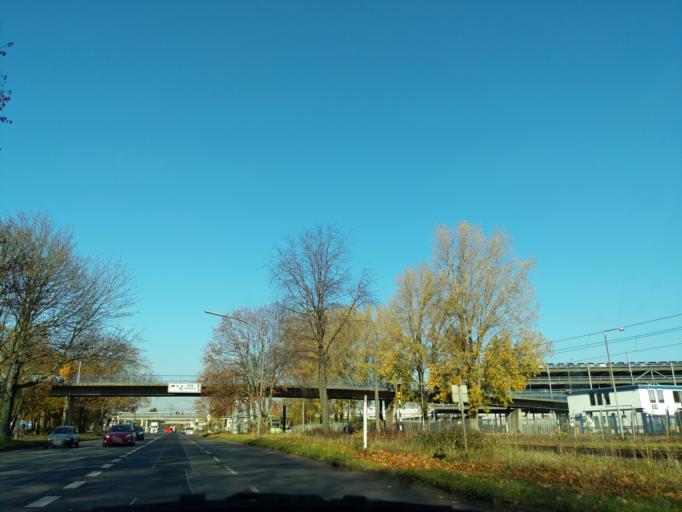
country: DE
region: North Rhine-Westphalia
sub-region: Regierungsbezirk Koln
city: Leverkusen
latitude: 51.0155
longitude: 6.9551
